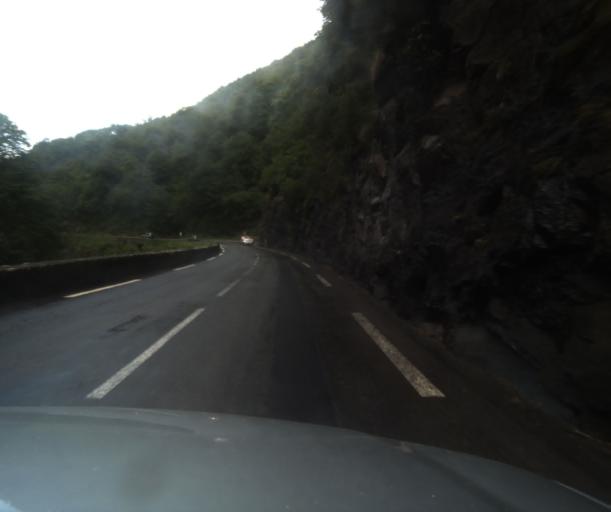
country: FR
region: Midi-Pyrenees
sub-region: Departement des Hautes-Pyrenees
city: Pierrefitte-Nestalas
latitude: 42.9358
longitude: -0.0485
